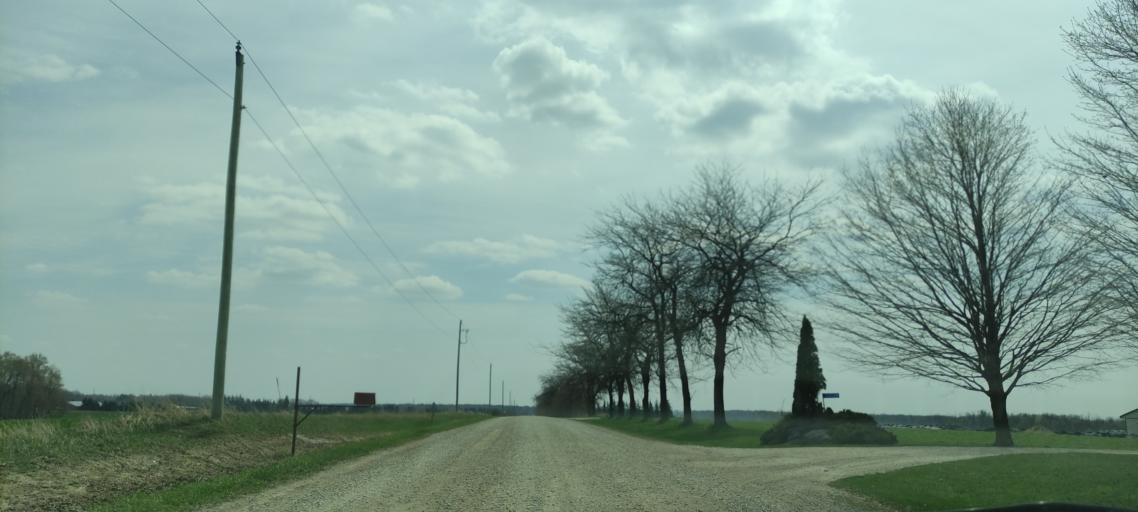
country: CA
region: Ontario
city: Stratford
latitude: 43.3465
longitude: -80.7437
